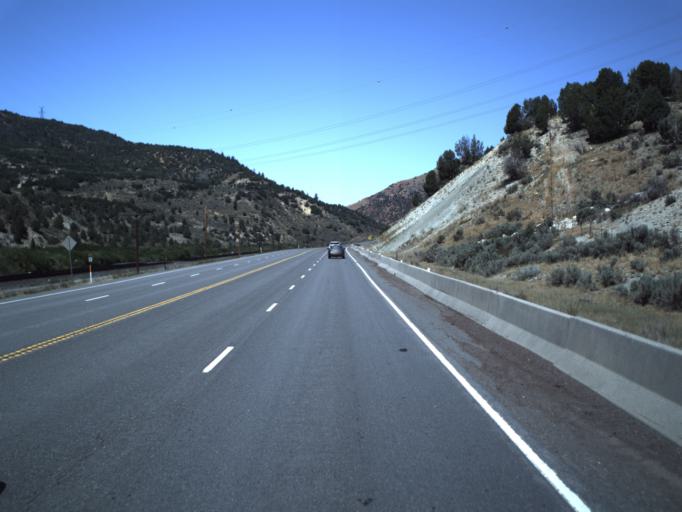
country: US
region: Utah
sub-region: Utah County
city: Mapleton
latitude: 39.9773
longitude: -111.3471
